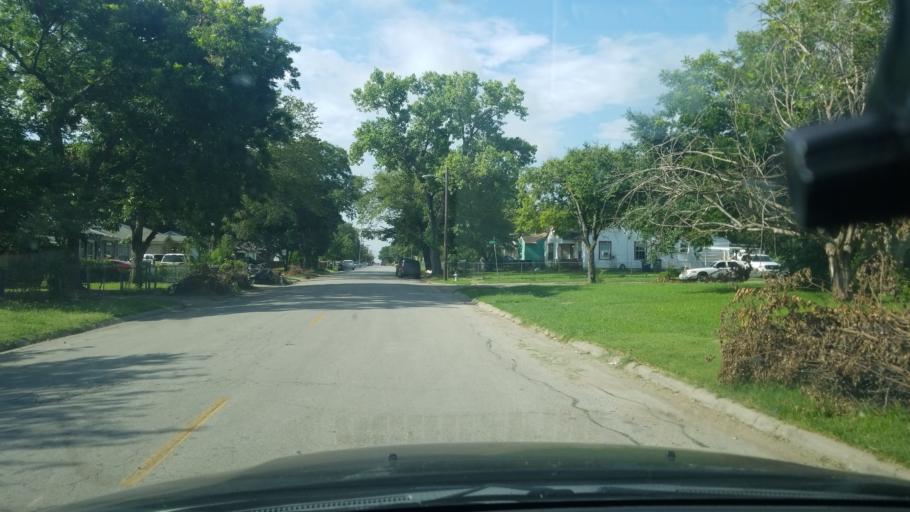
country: US
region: Texas
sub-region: Dallas County
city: Balch Springs
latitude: 32.7396
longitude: -96.6743
